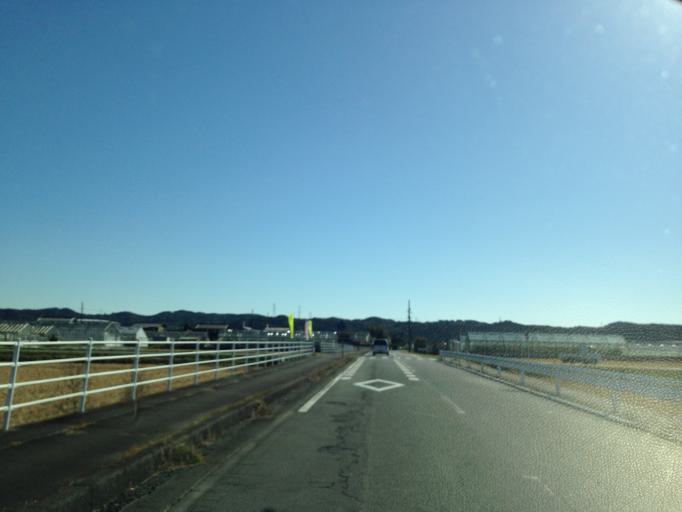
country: JP
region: Shizuoka
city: Fukuroi
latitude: 34.7587
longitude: 137.9511
